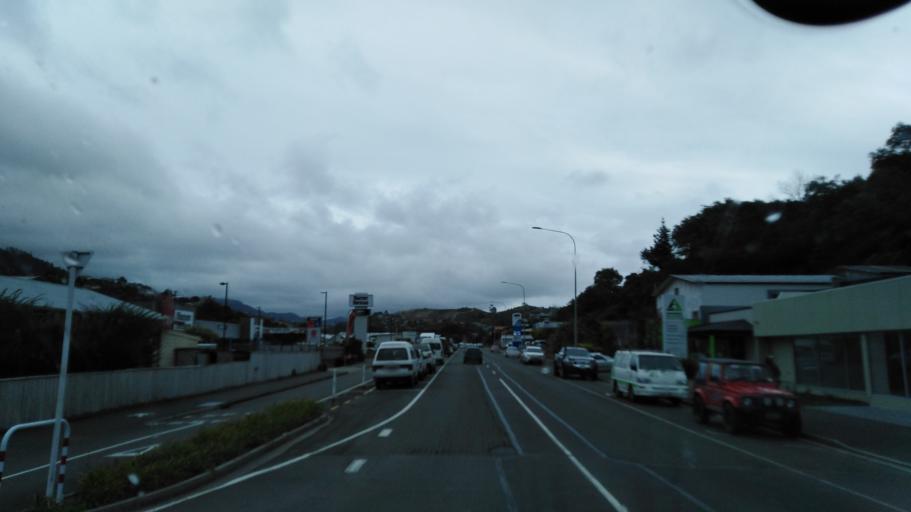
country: NZ
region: Nelson
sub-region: Nelson City
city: Nelson
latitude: -41.2746
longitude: 173.2754
